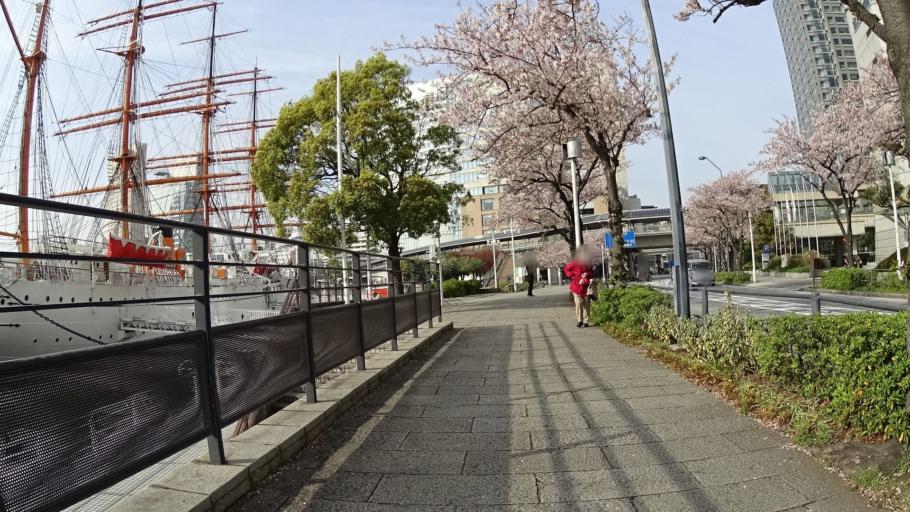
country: JP
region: Kanagawa
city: Yokohama
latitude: 35.4543
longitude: 139.6324
